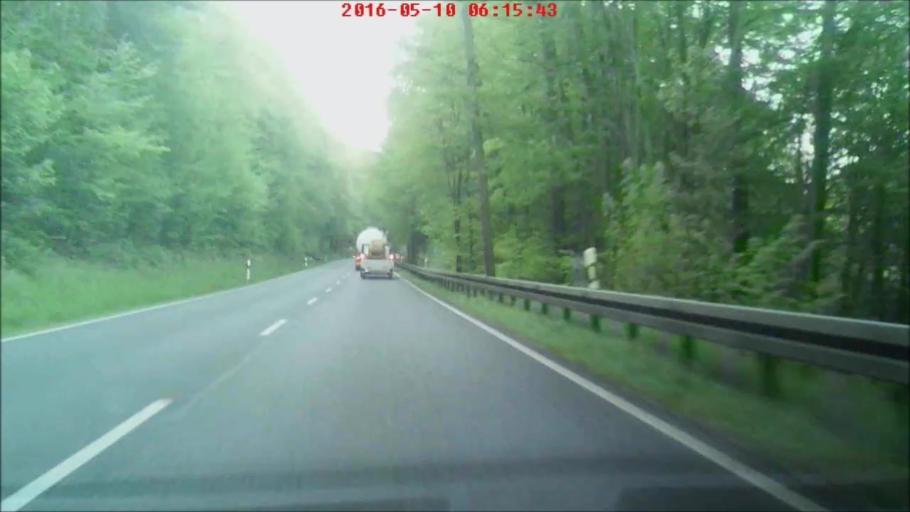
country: DE
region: Hesse
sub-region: Regierungsbezirk Kassel
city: Burghaun
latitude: 50.7494
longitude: 9.6841
